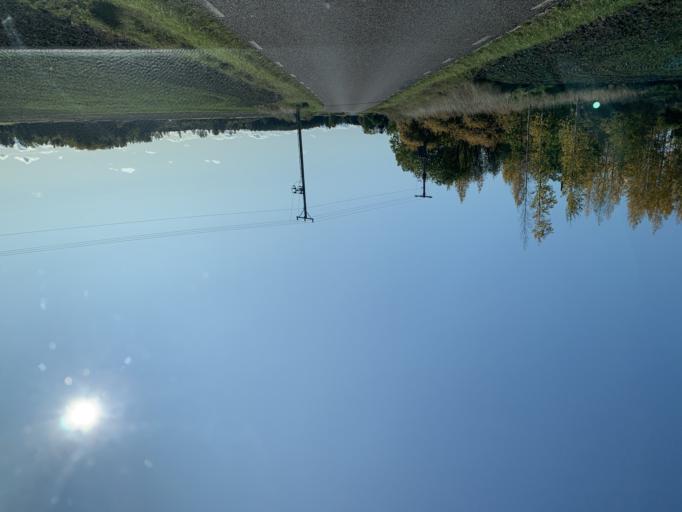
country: SE
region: Soedermanland
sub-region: Eskilstuna Kommun
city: Kvicksund
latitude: 59.5081
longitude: 16.3472
